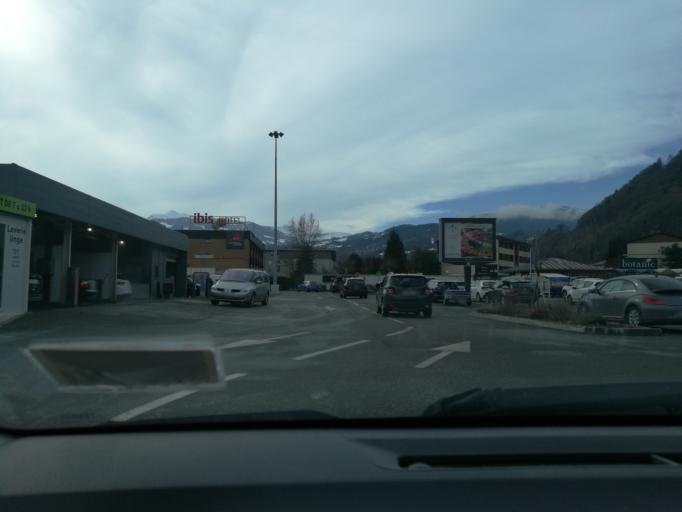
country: FR
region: Rhone-Alpes
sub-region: Departement de la Haute-Savoie
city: Sallanches
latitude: 45.9522
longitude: 6.6289
